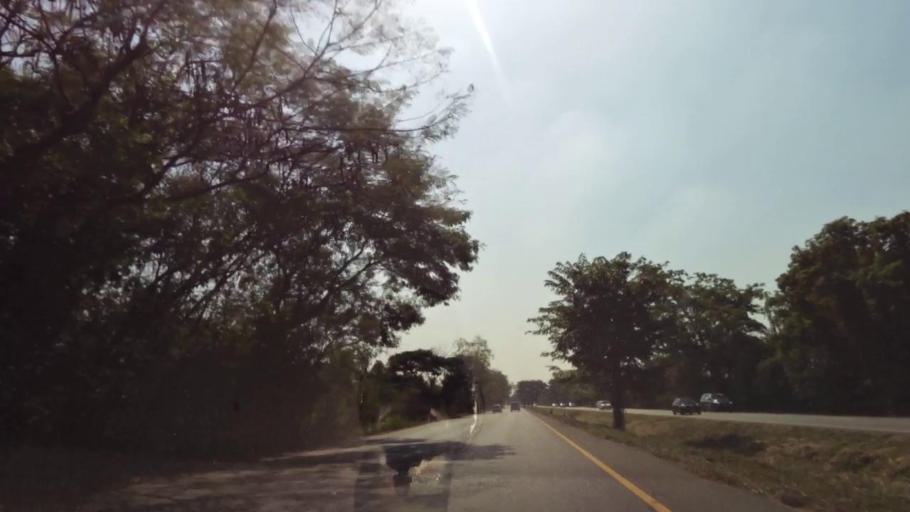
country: TH
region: Phichit
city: Wachira Barami
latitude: 16.3695
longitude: 100.1323
